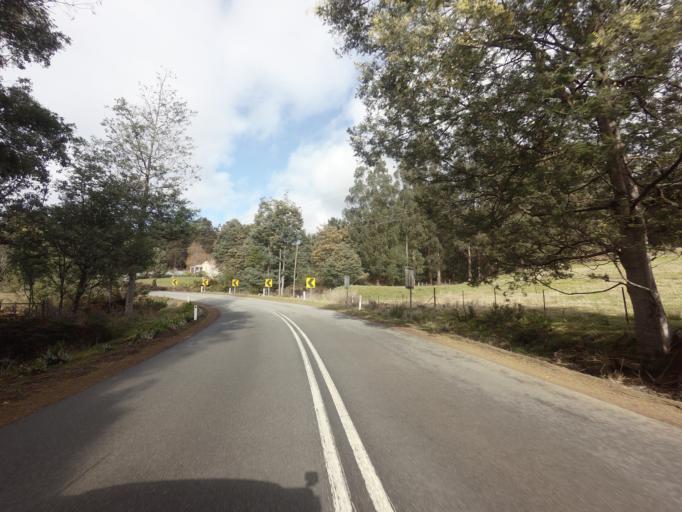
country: AU
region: Tasmania
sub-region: Huon Valley
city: Geeveston
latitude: -43.3602
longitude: 146.9586
